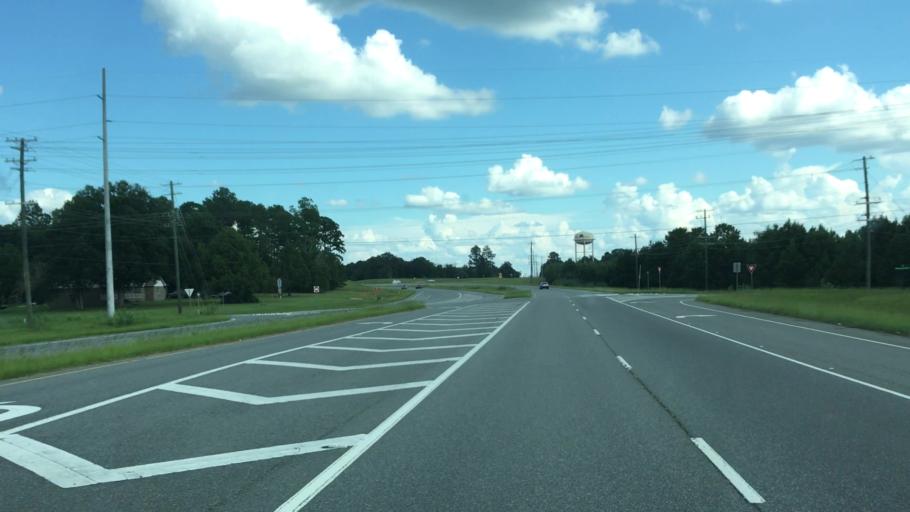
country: US
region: Georgia
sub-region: Laurens County
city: Dublin
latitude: 32.5045
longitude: -82.9437
